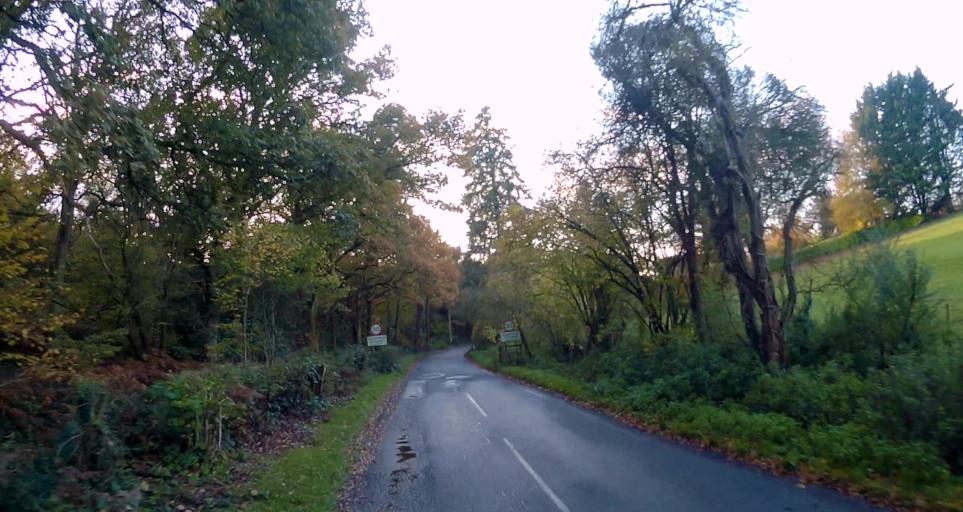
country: GB
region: England
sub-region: Hampshire
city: Basingstoke
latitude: 51.1913
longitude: -1.0877
